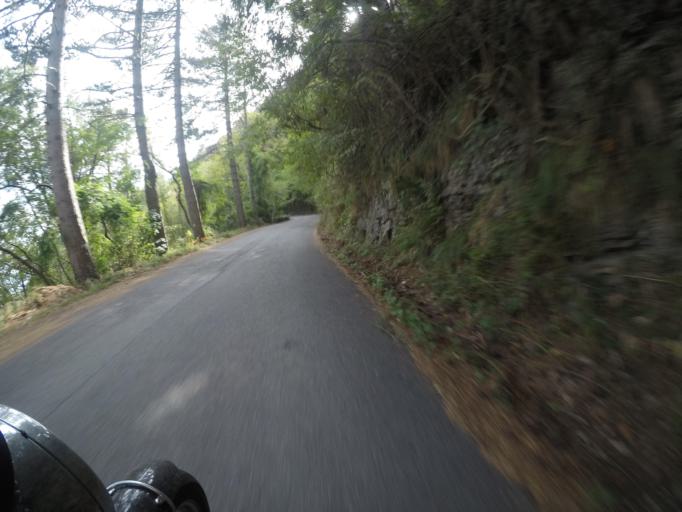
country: IT
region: Tuscany
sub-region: Provincia di Massa-Carrara
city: Fosdinovo
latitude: 44.1232
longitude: 10.0853
